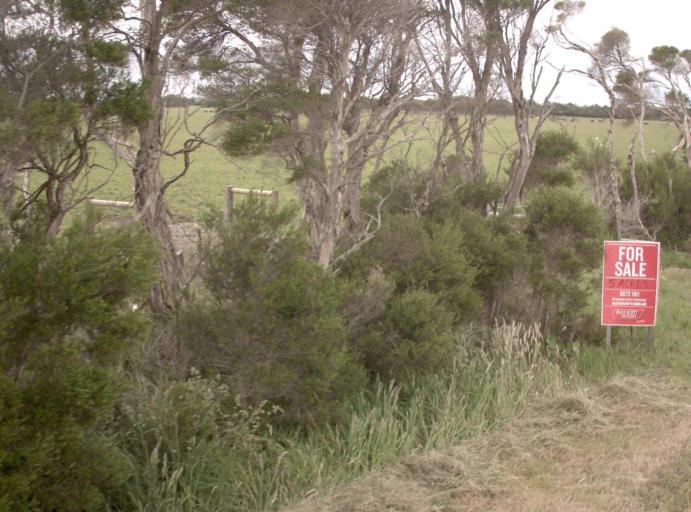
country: AU
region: Victoria
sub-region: Bass Coast
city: North Wonthaggi
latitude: -38.5635
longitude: 145.6334
